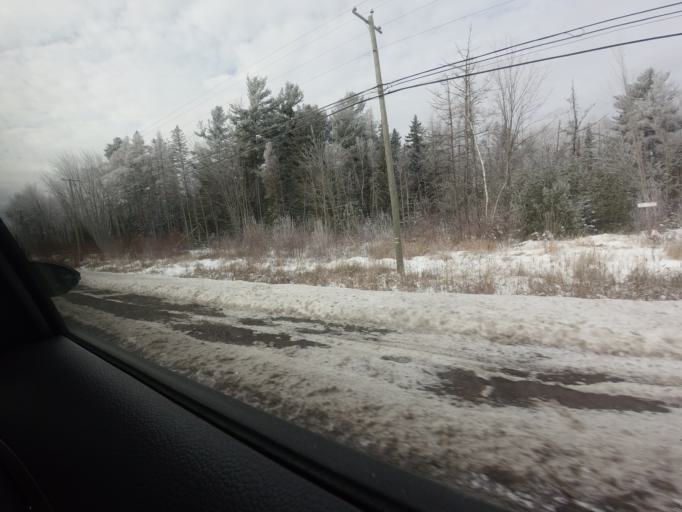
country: CA
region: New Brunswick
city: Oromocto
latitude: 45.8583
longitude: -66.4533
